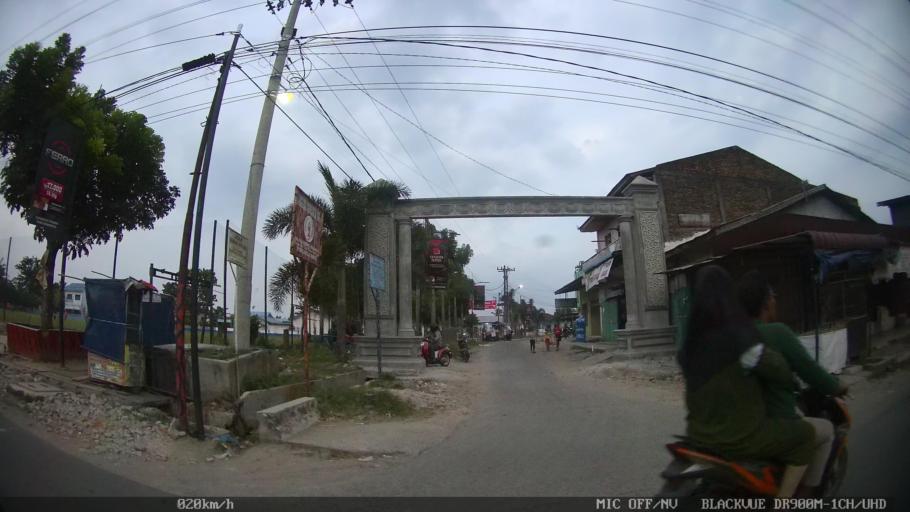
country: ID
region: North Sumatra
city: Sunggal
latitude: 3.5799
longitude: 98.5907
